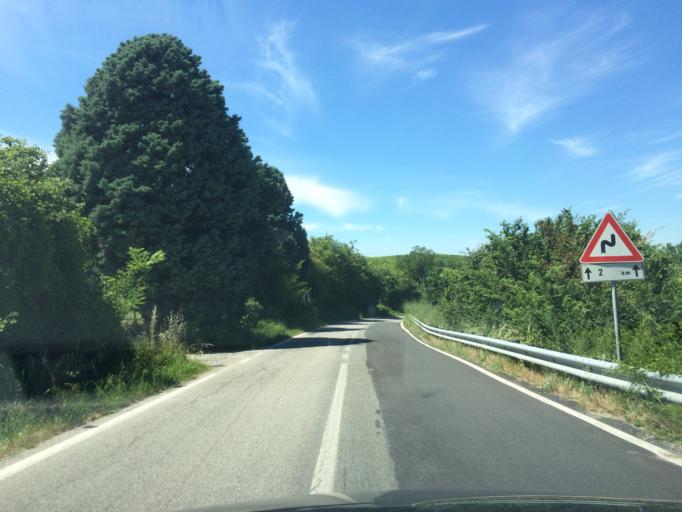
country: IT
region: Piedmont
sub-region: Provincia di Asti
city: Castel Boglione
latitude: 44.7324
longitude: 8.3913
